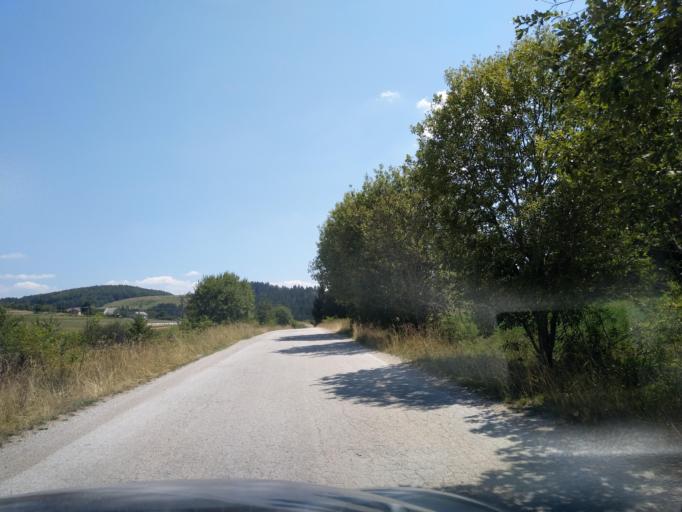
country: RS
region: Central Serbia
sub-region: Zlatiborski Okrug
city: Nova Varos
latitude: 43.4656
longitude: 19.9728
